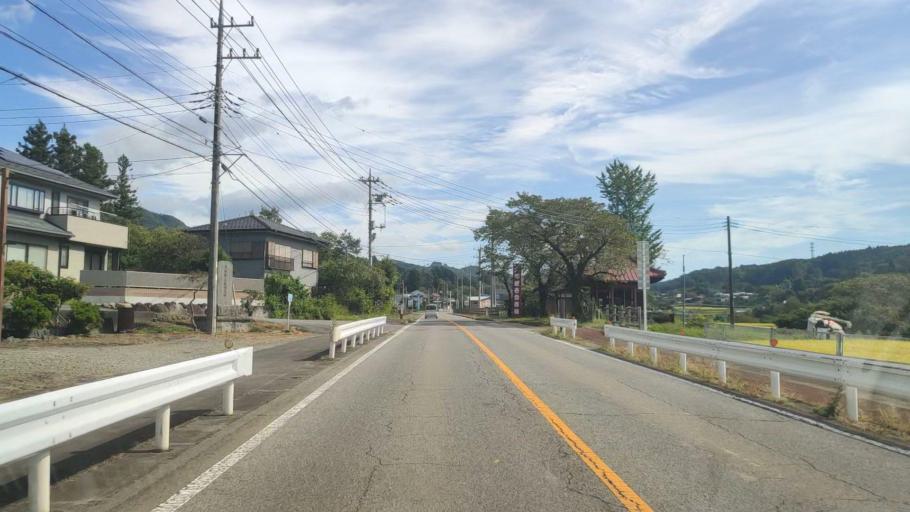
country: JP
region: Gunma
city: Nakanojomachi
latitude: 36.6159
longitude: 138.8921
